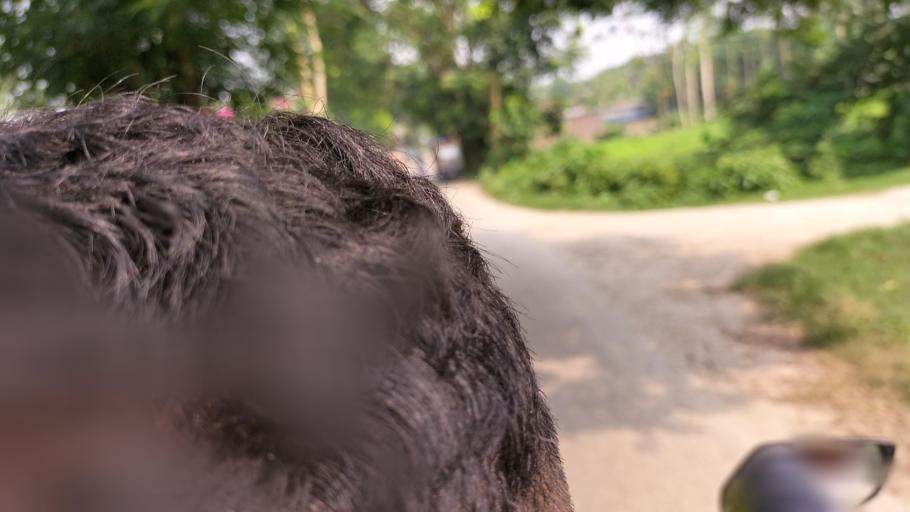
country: BD
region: Dhaka
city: Azimpur
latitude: 23.6914
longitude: 90.2997
